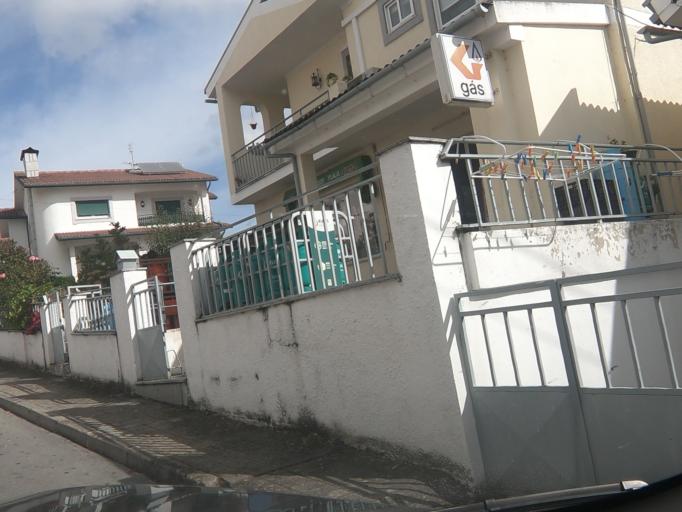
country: PT
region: Vila Real
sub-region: Vila Real
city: Vila Real
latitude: 41.2930
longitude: -7.7296
